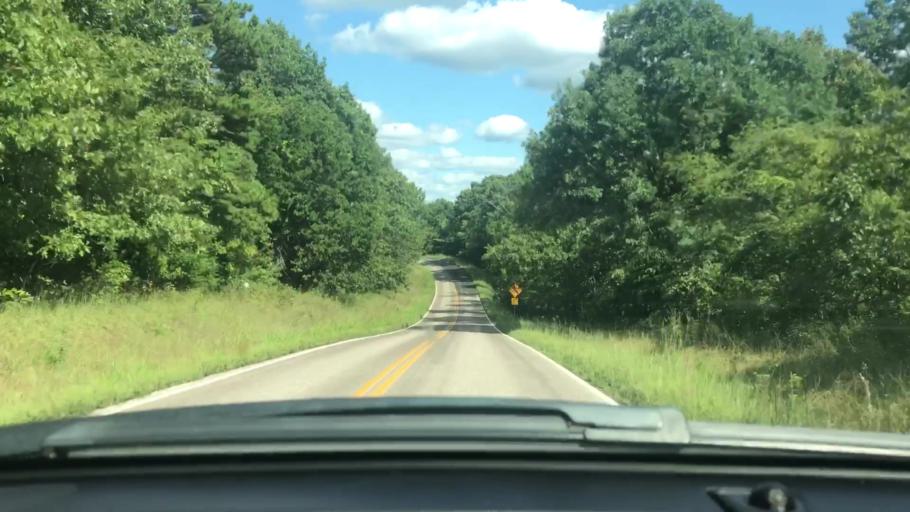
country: US
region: Missouri
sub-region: Wright County
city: Hartville
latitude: 37.3764
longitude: -92.3740
